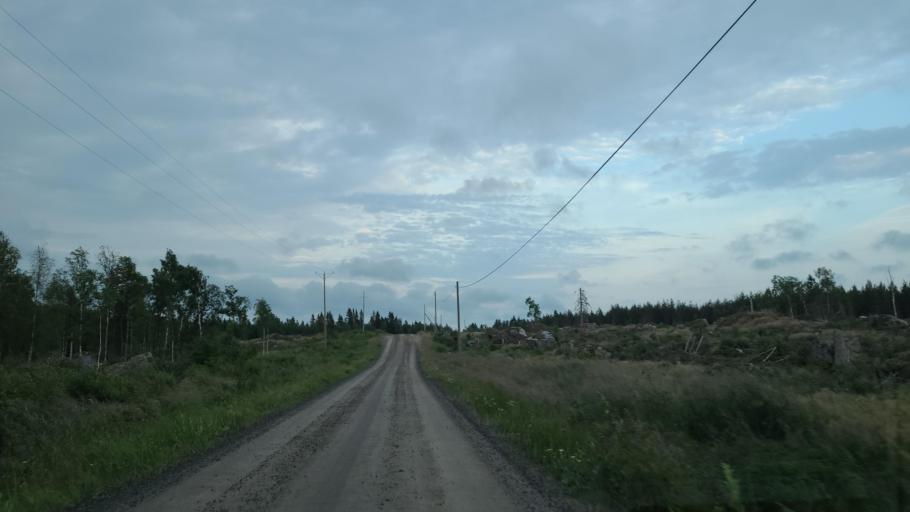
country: FI
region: Ostrobothnia
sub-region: Vaasa
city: Replot
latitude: 63.3187
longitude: 21.1494
